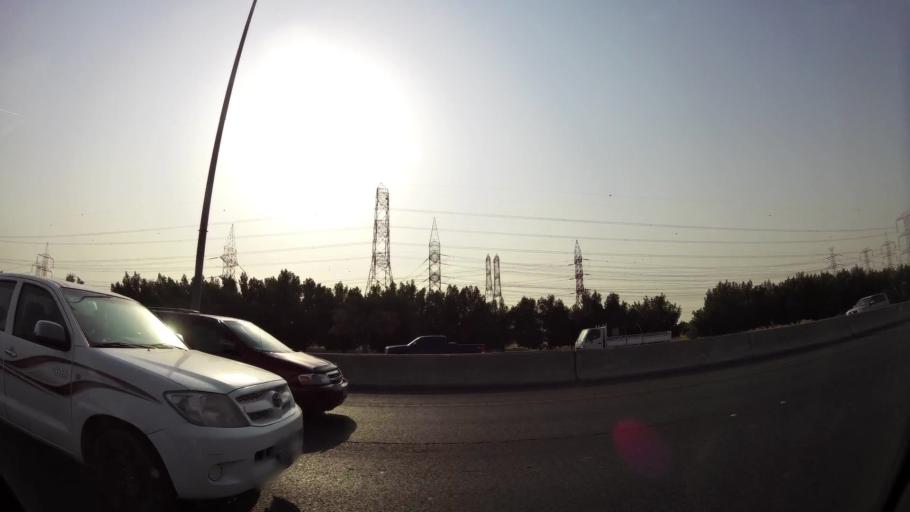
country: KW
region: Mubarak al Kabir
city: Sabah as Salim
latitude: 29.2221
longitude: 48.0550
